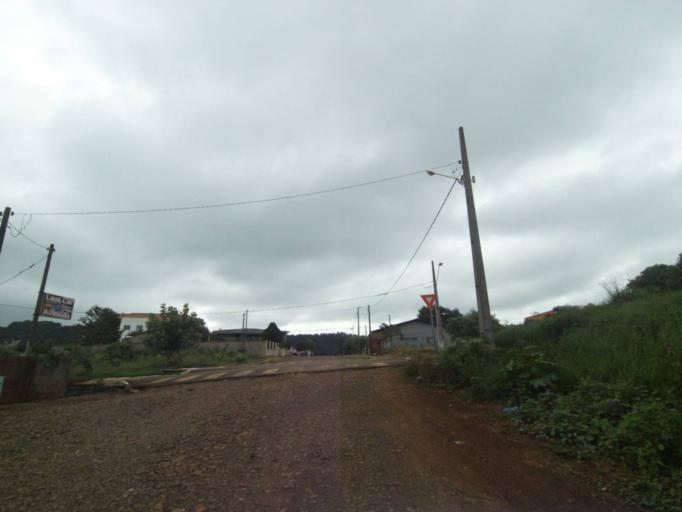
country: BR
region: Parana
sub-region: Pitanga
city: Pitanga
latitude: -24.9365
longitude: -51.8724
